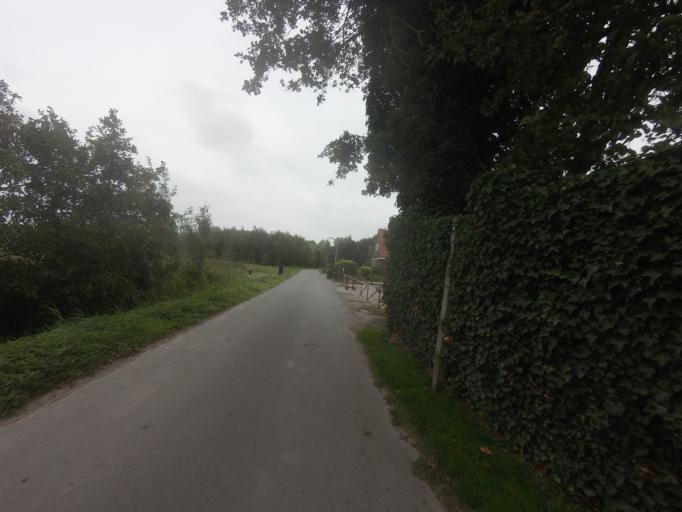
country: NL
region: Friesland
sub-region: Gemeente Leeuwarden
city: Bilgaard
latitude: 53.2235
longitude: 5.7904
